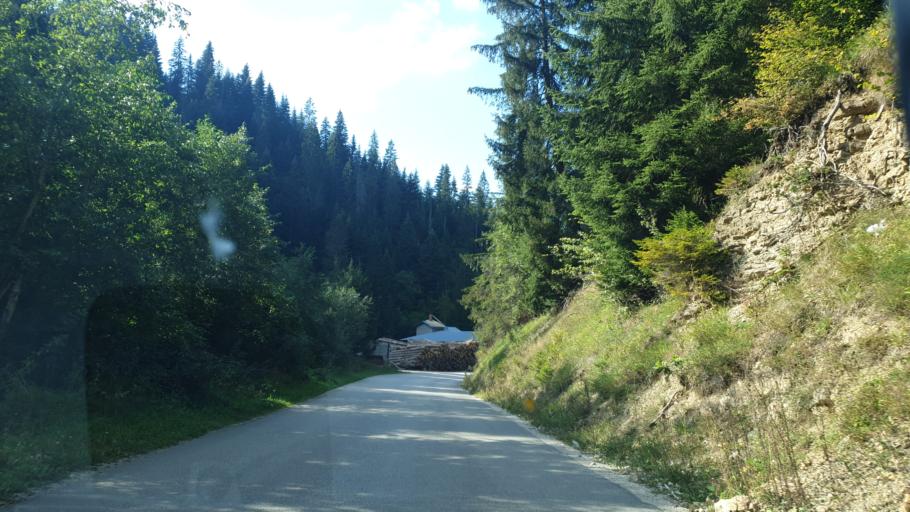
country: RS
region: Central Serbia
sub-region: Zlatiborski Okrug
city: Nova Varos
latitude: 43.4466
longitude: 19.8495
